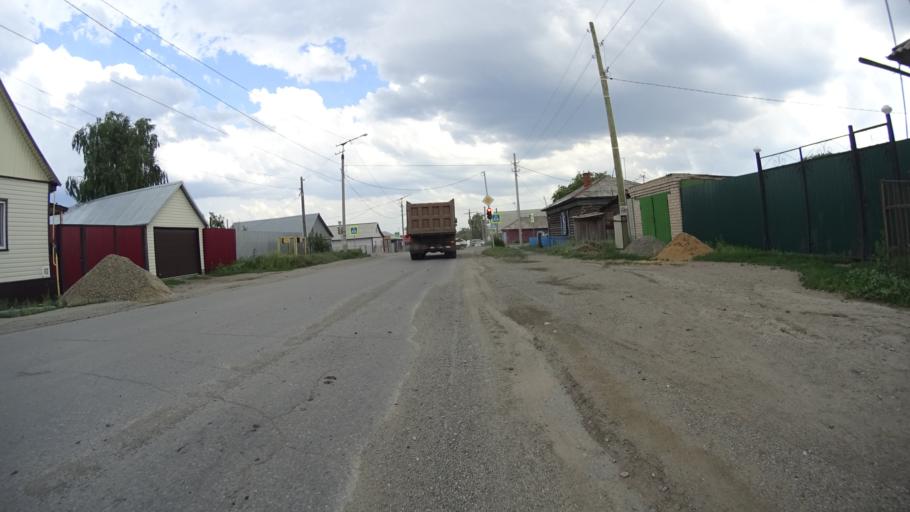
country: RU
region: Chelyabinsk
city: Troitsk
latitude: 54.0983
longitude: 61.5912
